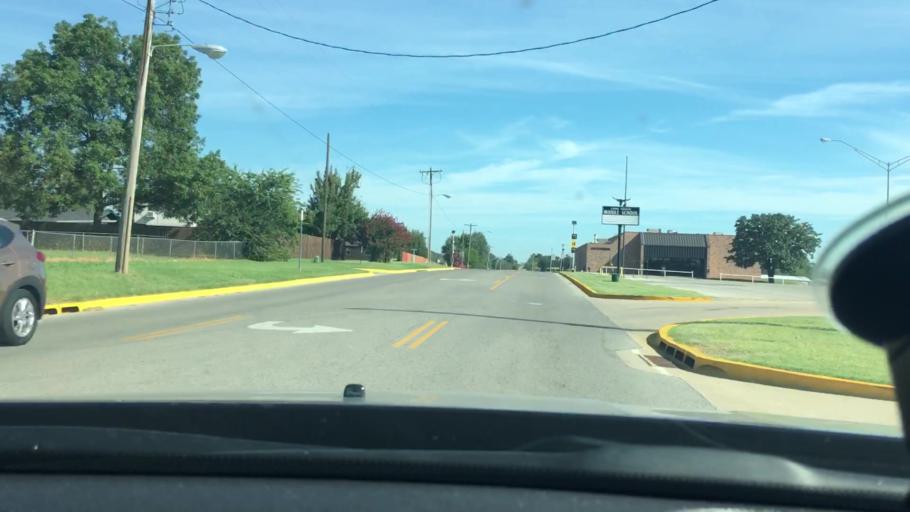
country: US
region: Oklahoma
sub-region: Carter County
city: Lone Grove
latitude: 34.1770
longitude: -97.2474
